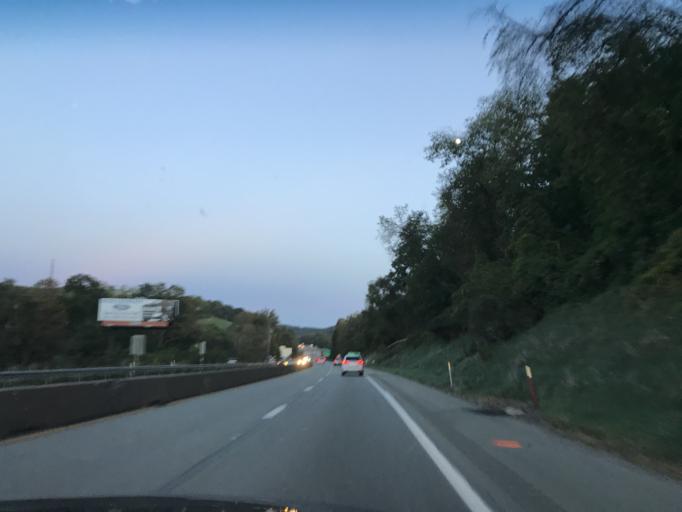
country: US
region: Pennsylvania
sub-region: Washington County
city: North Charleroi
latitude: 40.1172
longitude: -79.9484
